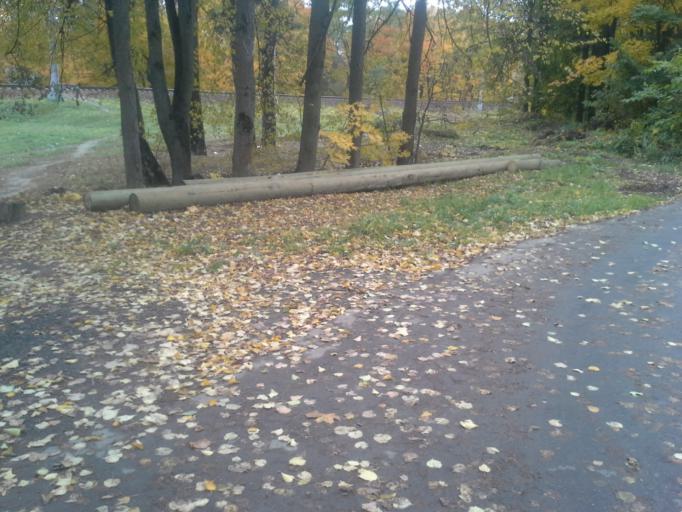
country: RU
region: Moscow
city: Solntsevo
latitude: 55.6568
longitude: 37.3643
